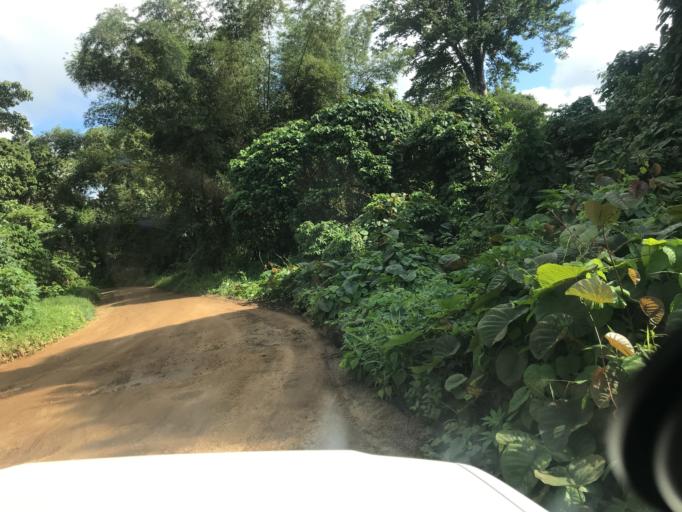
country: VU
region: Sanma
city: Luganville
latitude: -15.5061
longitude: 167.1038
